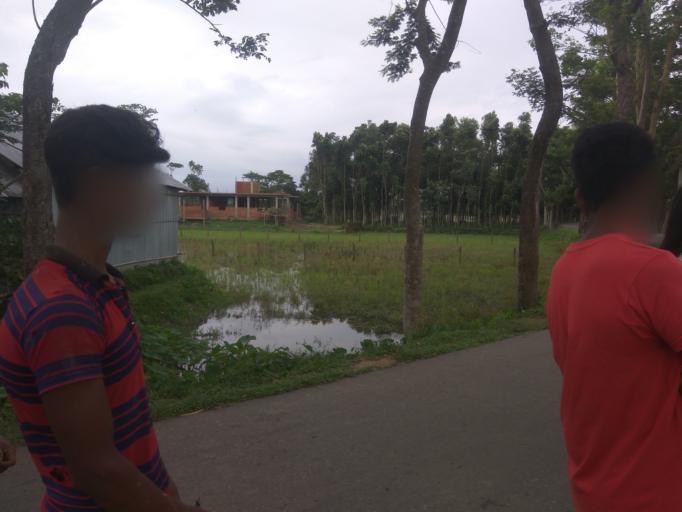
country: IN
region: Assam
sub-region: Karimganj
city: Karimganj
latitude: 24.8245
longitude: 92.2269
